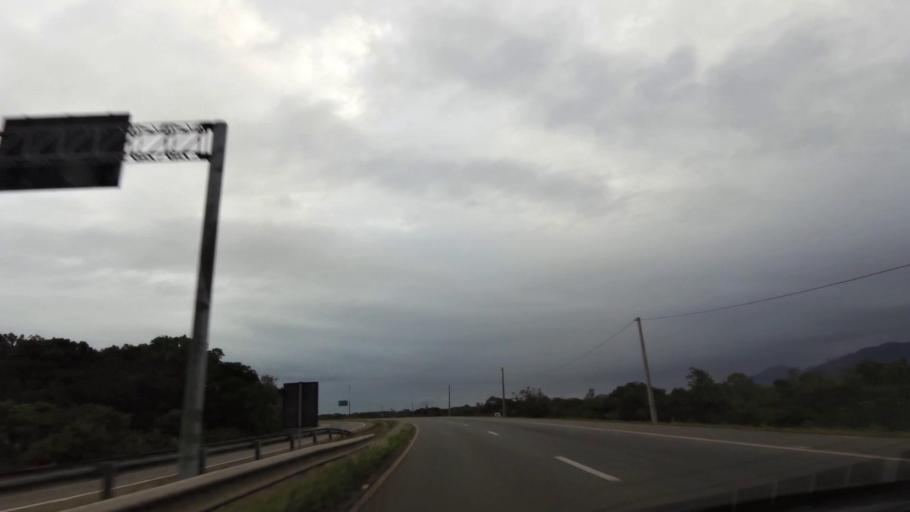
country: BR
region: Espirito Santo
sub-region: Guarapari
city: Guarapari
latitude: -20.5857
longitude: -40.4231
